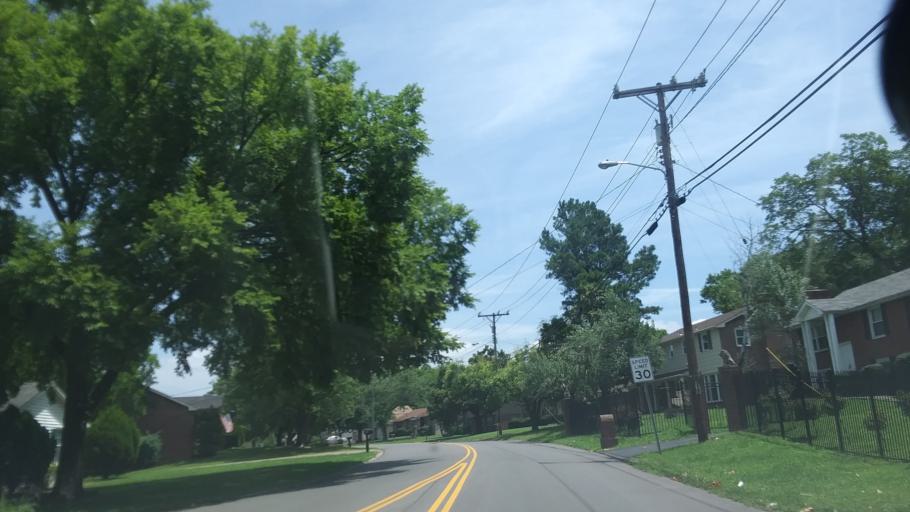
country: US
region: Tennessee
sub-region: Rutherford County
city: La Vergne
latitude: 36.0684
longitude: -86.6298
